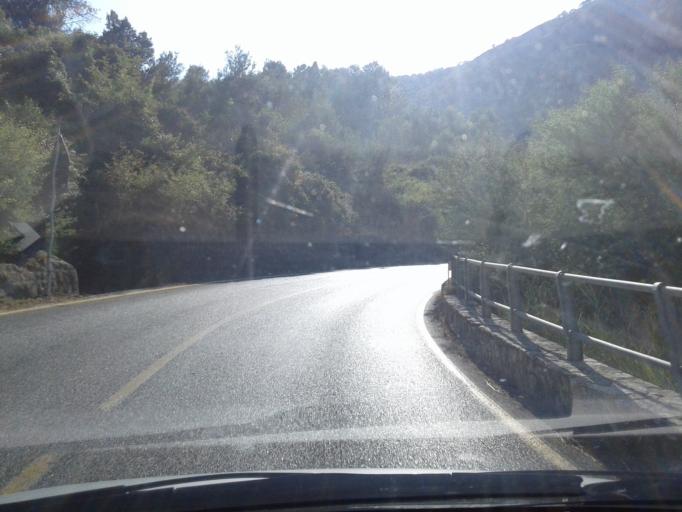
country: IT
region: Sicily
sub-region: Palermo
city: Pollina
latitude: 38.0112
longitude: 14.1032
